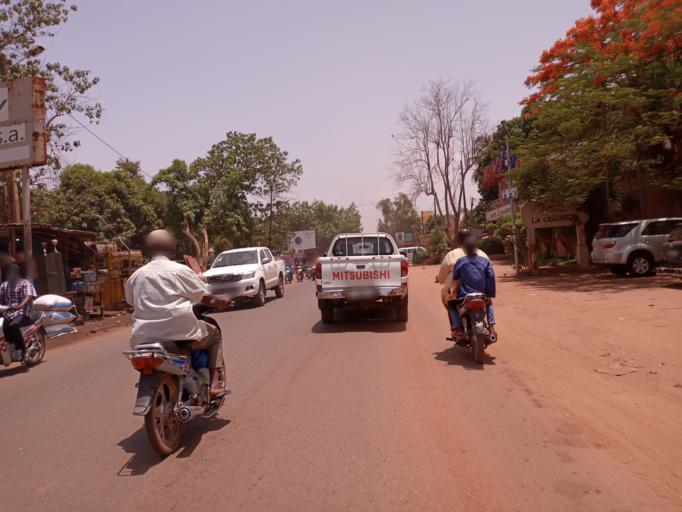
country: ML
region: Bamako
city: Bamako
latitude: 12.6486
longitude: -7.9759
